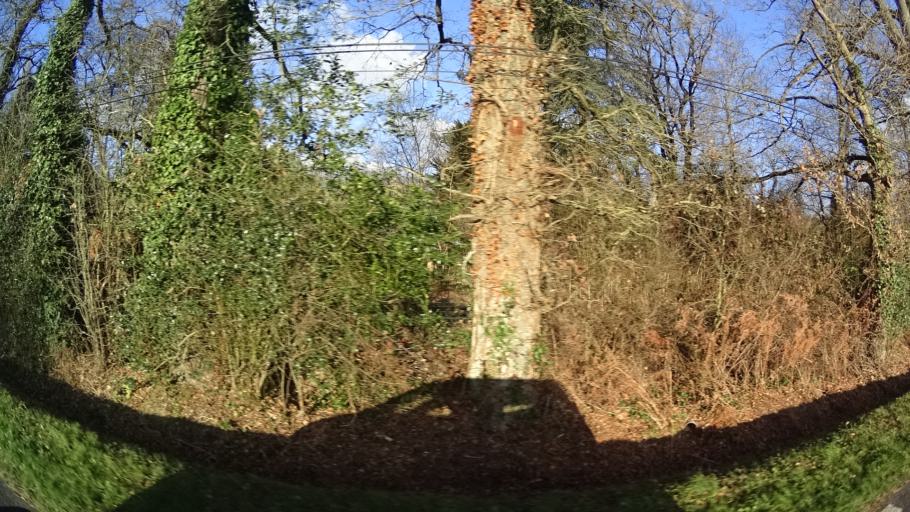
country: FR
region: Pays de la Loire
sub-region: Departement de la Loire-Atlantique
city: Plesse
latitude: 47.5298
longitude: -1.9057
